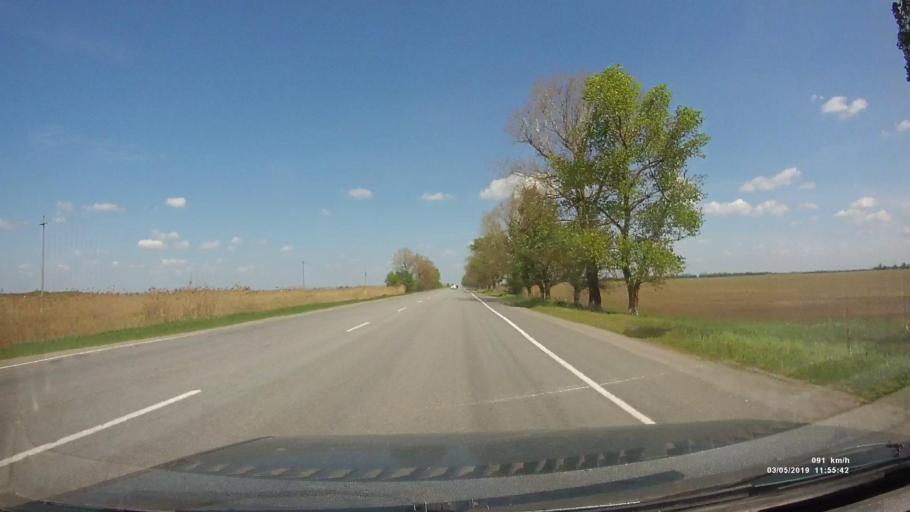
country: RU
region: Rostov
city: Bagayevskaya
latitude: 47.1845
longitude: 40.2936
